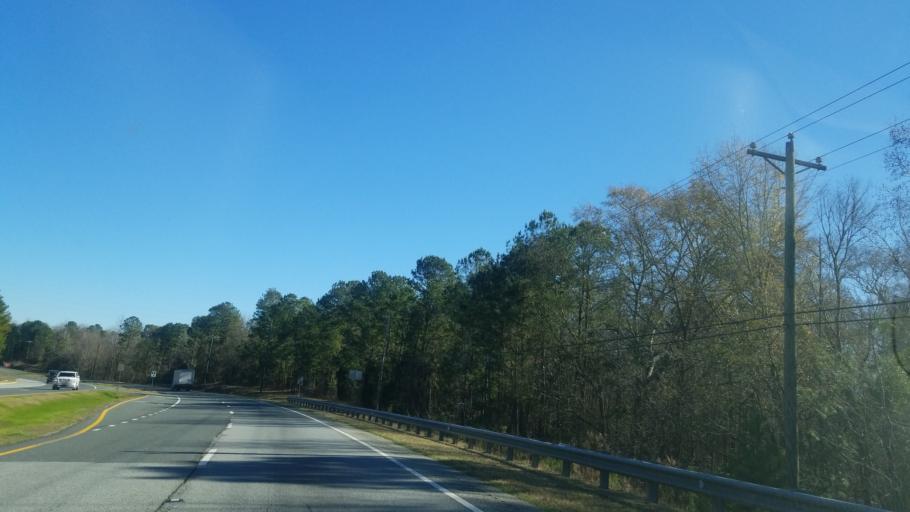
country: US
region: Georgia
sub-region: Muscogee County
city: Columbus
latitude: 32.5409
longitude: -84.8193
